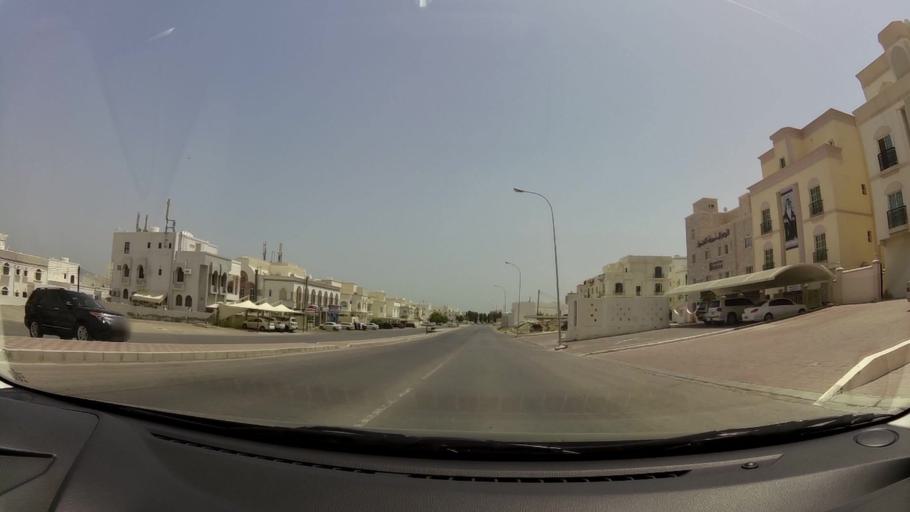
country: OM
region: Muhafazat Masqat
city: Bawshar
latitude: 23.5860
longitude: 58.4396
